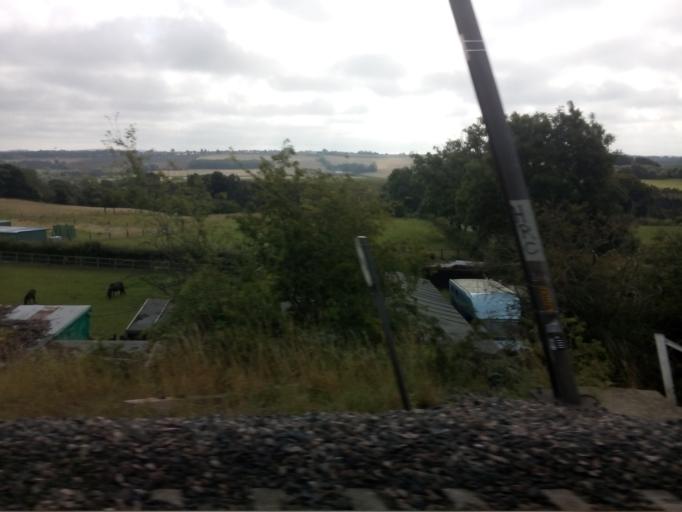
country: GB
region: England
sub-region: County Durham
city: Chester-le-Street
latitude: 54.8398
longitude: -1.5817
